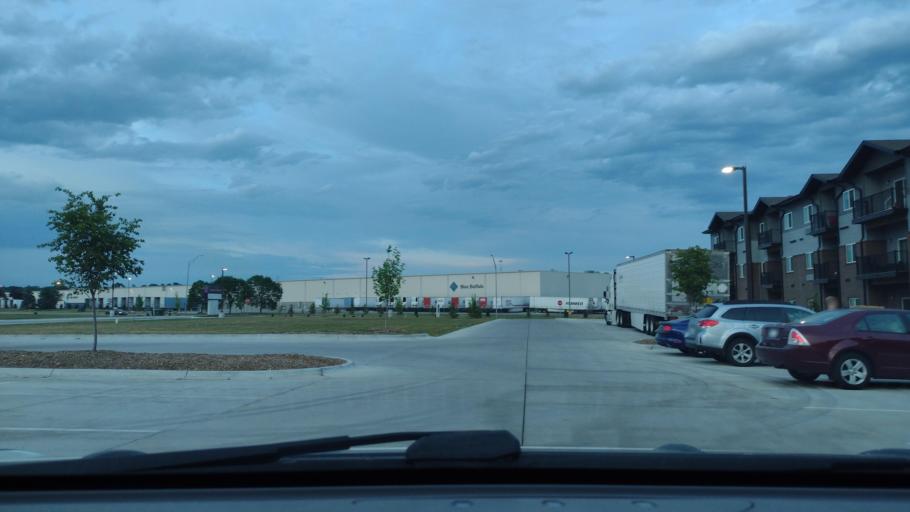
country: US
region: Nebraska
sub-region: Sarpy County
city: Offutt Air Force Base
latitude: 41.1533
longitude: -95.9365
